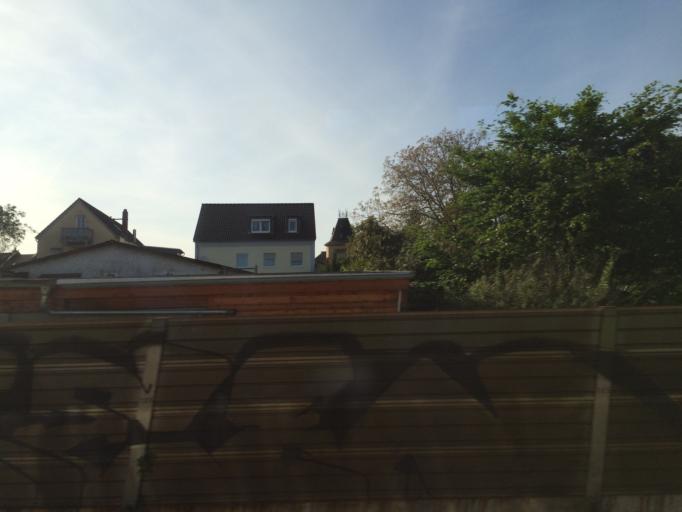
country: DE
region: Hesse
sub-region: Regierungsbezirk Darmstadt
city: Eltville
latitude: 50.0268
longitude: 8.1157
